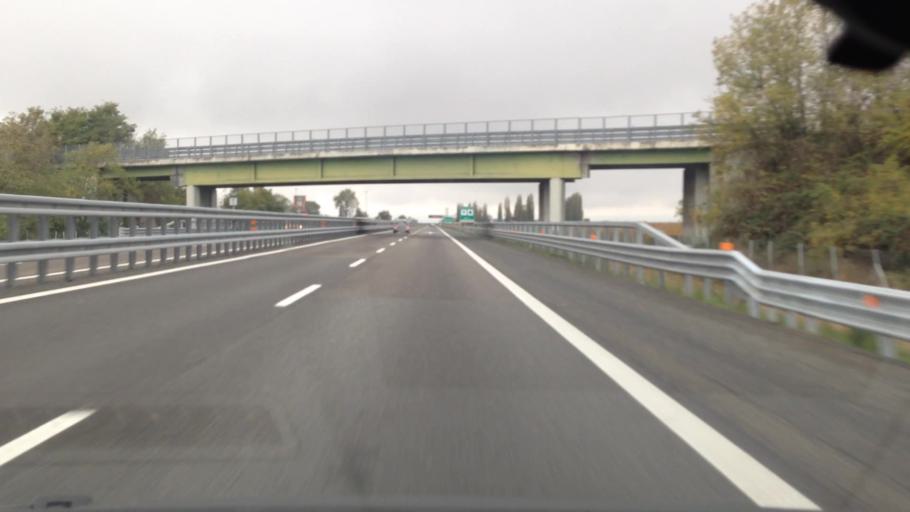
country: IT
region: Piedmont
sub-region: Provincia di Asti
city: San Paolo Solbrito
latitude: 44.9488
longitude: 7.9621
